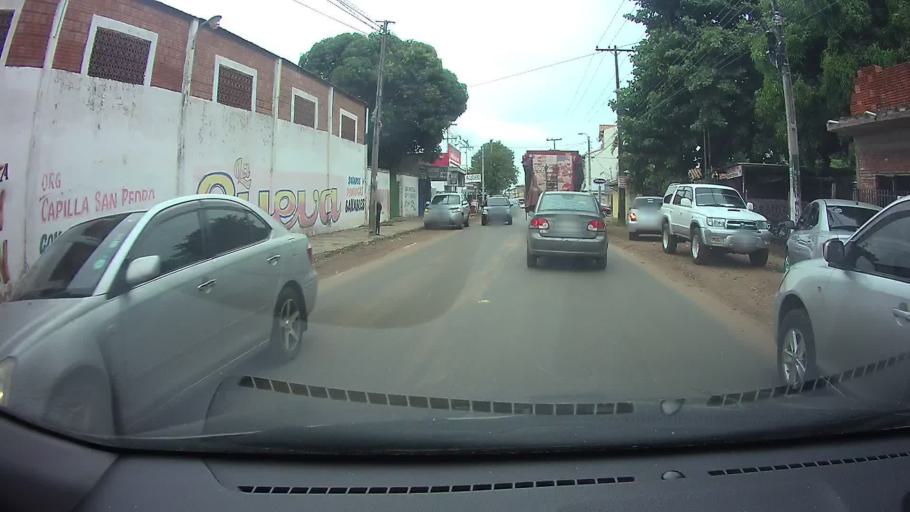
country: PY
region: Central
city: San Lorenzo
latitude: -25.3217
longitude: -57.4976
